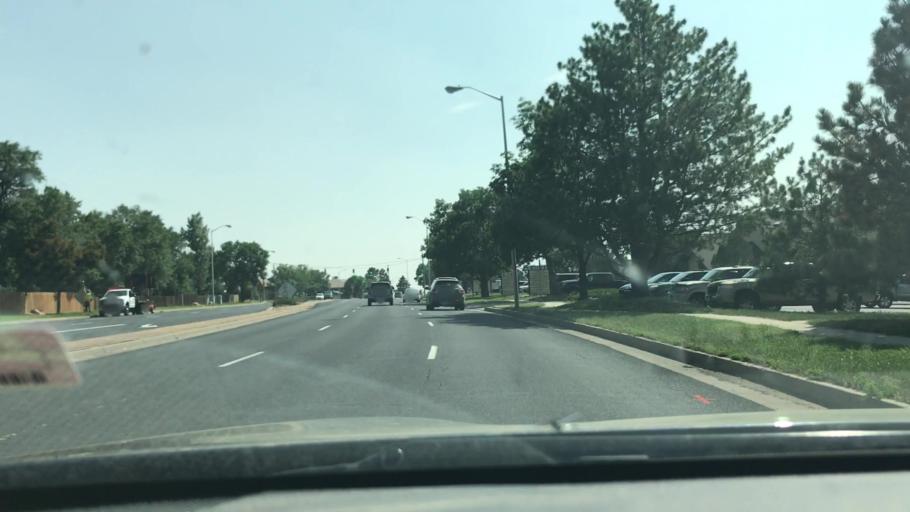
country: US
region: Colorado
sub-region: El Paso County
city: Black Forest
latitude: 38.9458
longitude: -104.7741
